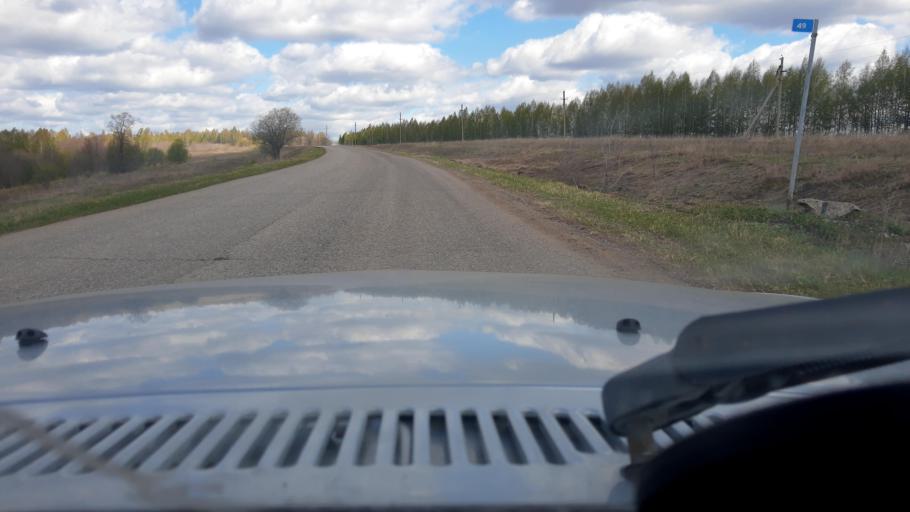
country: RU
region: Bashkortostan
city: Pavlovka
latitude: 55.3648
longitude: 56.4198
